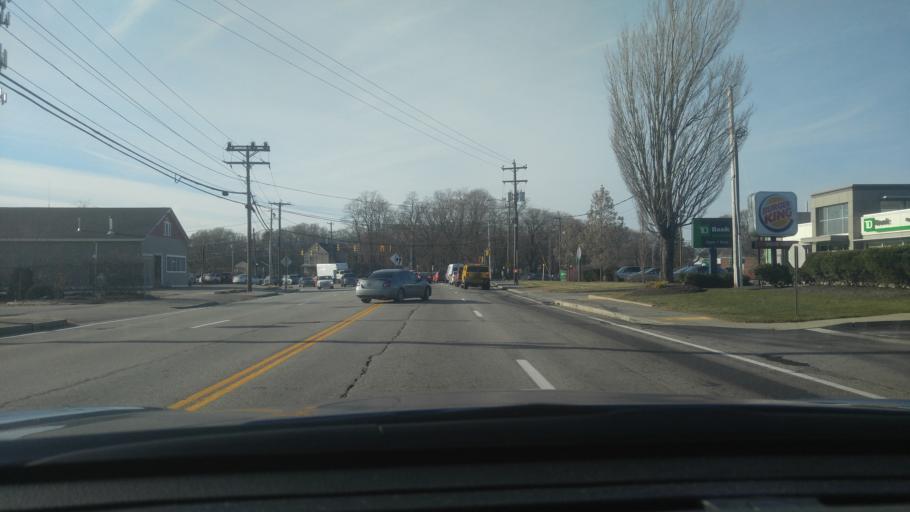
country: US
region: Rhode Island
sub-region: Kent County
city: Warwick
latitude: 41.7054
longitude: -71.4162
